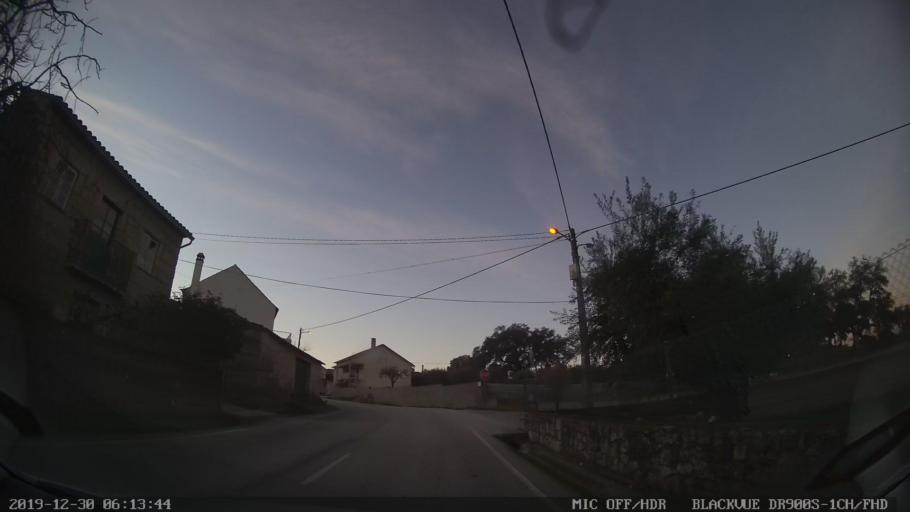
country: PT
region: Castelo Branco
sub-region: Penamacor
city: Penamacor
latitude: 40.1121
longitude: -7.2122
